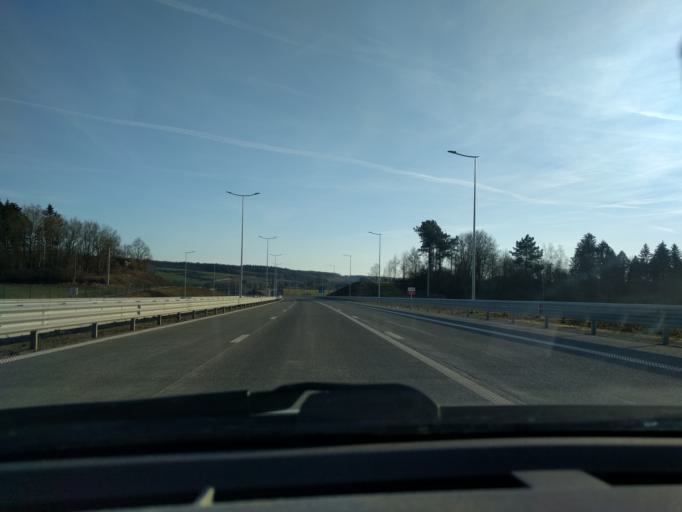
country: BE
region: Wallonia
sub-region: Province de Namur
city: Couvin
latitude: 50.0597
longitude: 4.5056
